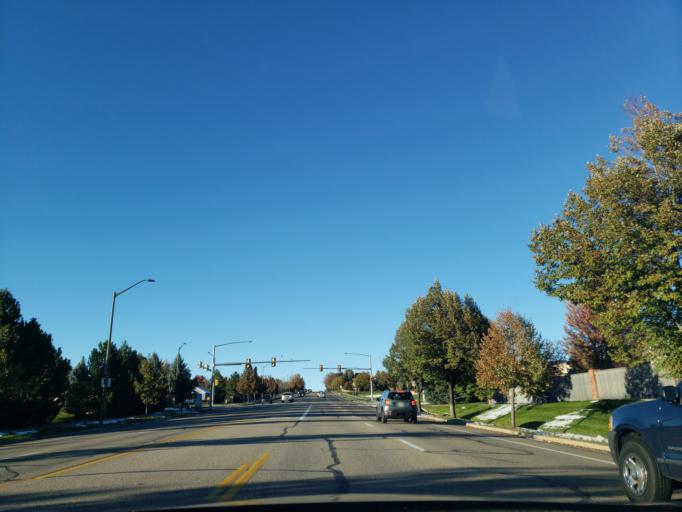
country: US
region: Colorado
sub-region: Larimer County
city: Fort Collins
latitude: 40.5082
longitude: -105.0581
